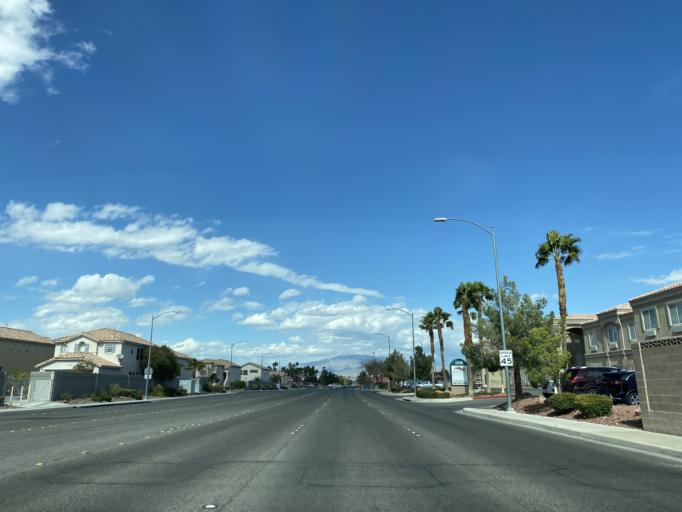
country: US
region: Nevada
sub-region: Clark County
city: Spring Valley
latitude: 36.2301
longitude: -115.2606
